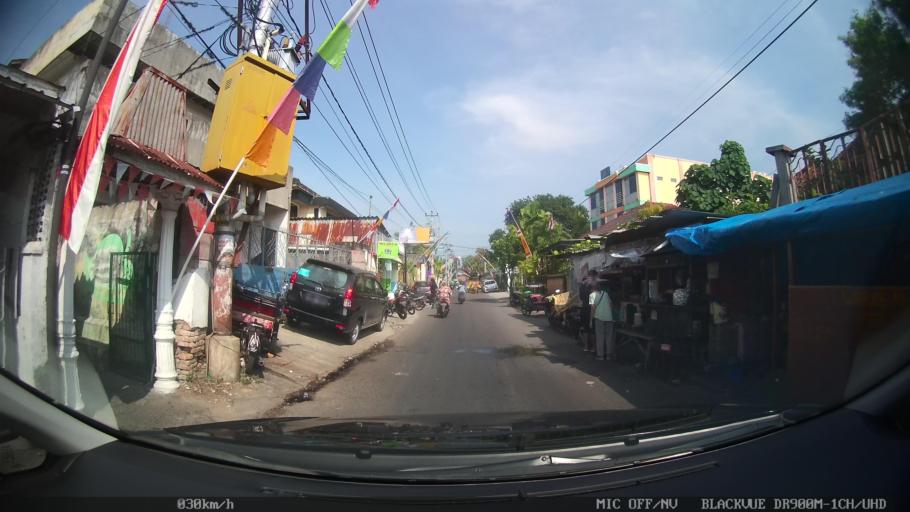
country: ID
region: Daerah Istimewa Yogyakarta
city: Yogyakarta
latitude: -7.7914
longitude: 110.3591
